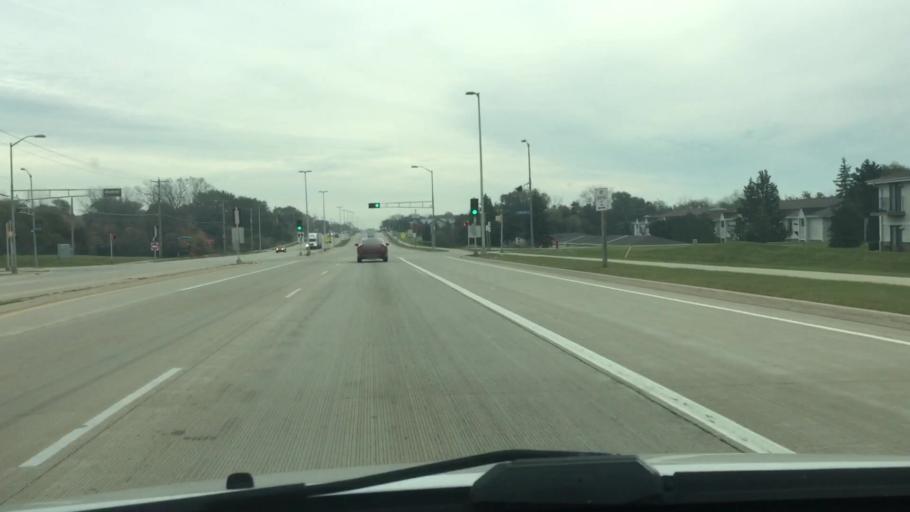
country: US
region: Wisconsin
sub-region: Milwaukee County
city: Franklin
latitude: 42.8726
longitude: -87.9683
